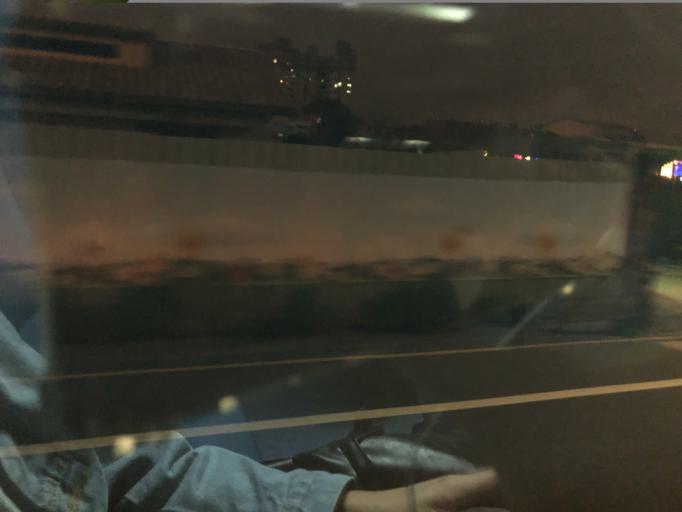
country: TW
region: Taiwan
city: Taoyuan City
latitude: 24.9925
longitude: 121.2857
